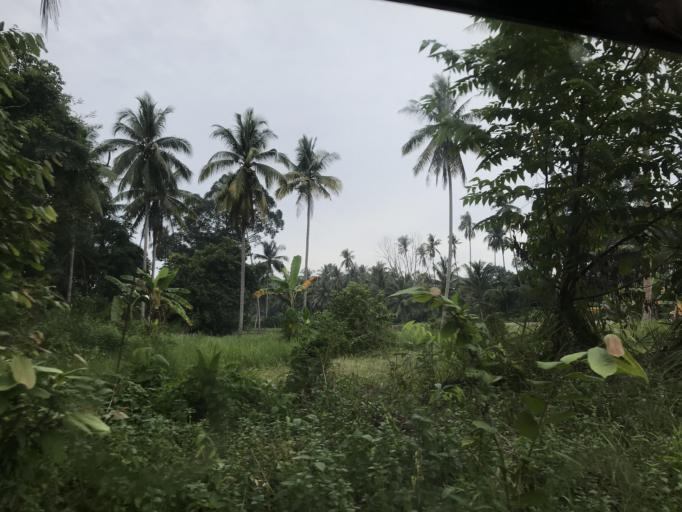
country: MY
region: Kelantan
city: Tumpat
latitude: 6.1659
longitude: 102.2000
